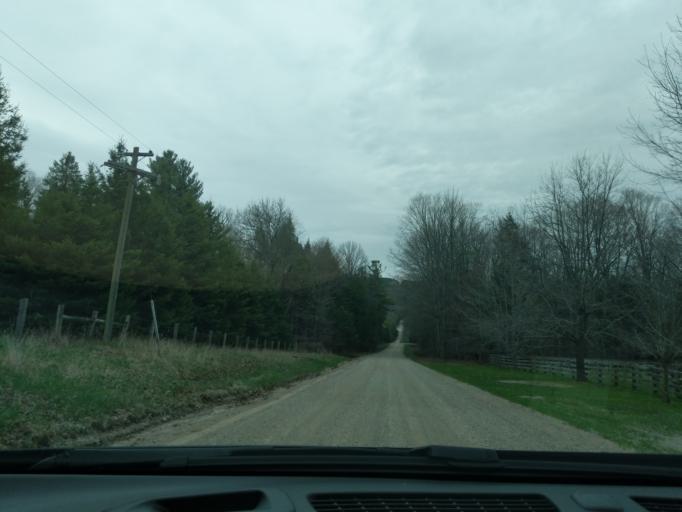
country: CA
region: Ontario
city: Orangeville
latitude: 44.0005
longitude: -80.0159
